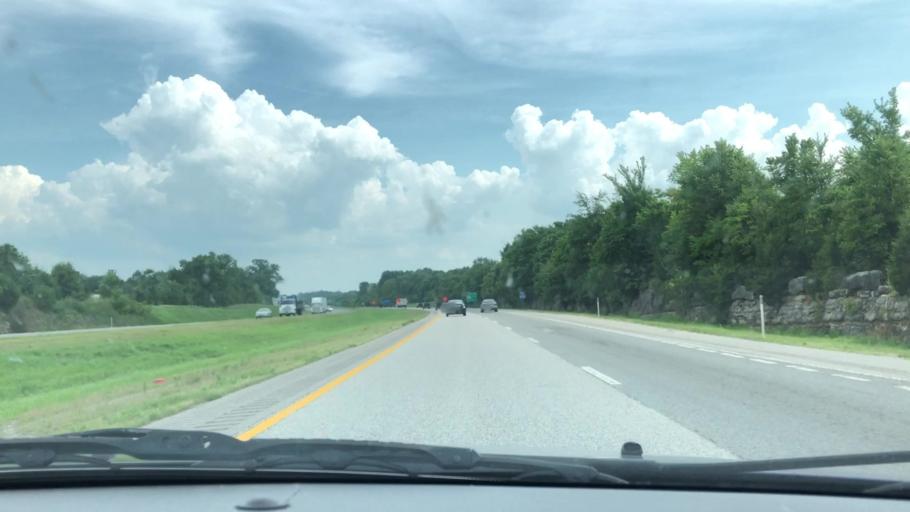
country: US
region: Tennessee
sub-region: Wilson County
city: Rural Hill
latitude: 36.0612
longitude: -86.4318
